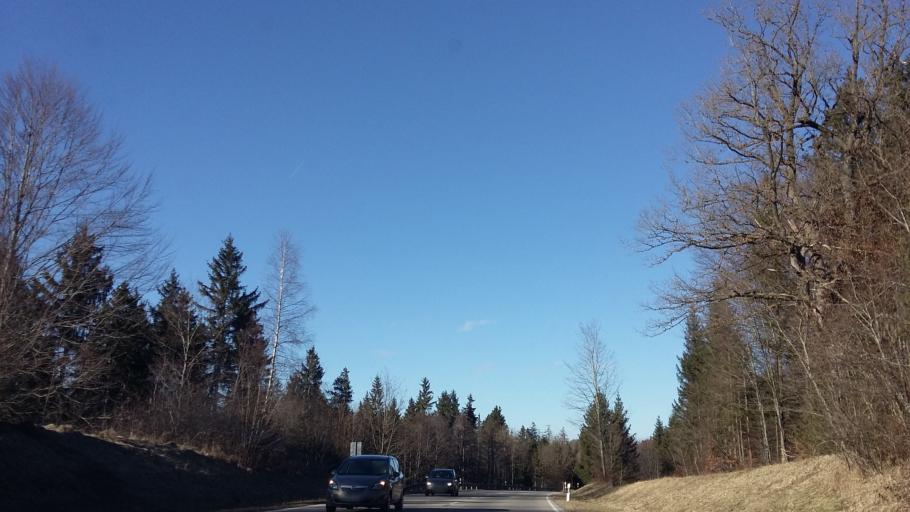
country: DE
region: Bavaria
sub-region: Upper Bavaria
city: Pocking
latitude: 47.9876
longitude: 11.3095
